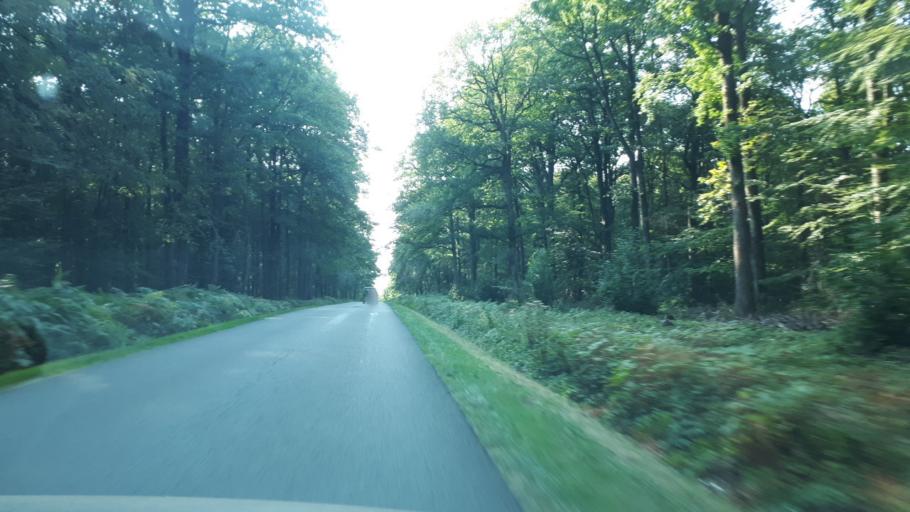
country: FR
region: Centre
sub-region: Departement du Cher
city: Saint-Eloy-de-Gy
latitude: 47.2187
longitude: 2.3543
